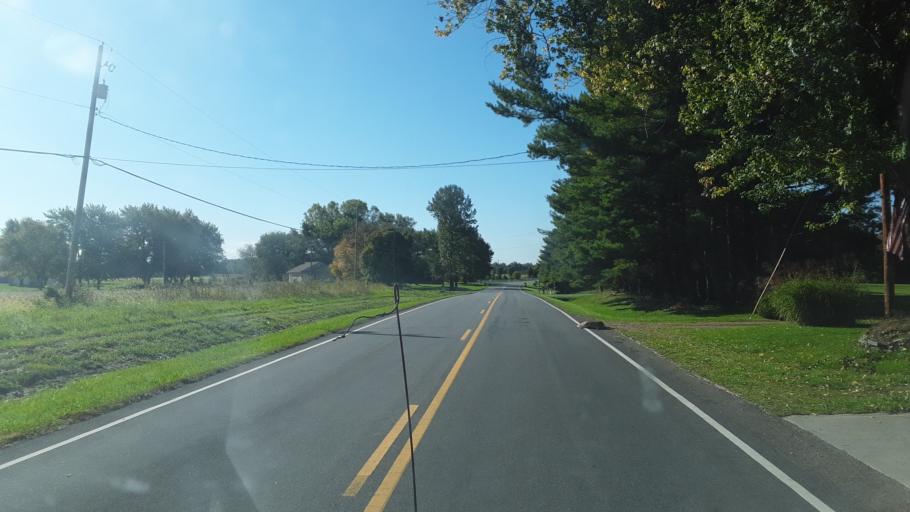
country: US
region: Ohio
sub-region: Delaware County
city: Sunbury
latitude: 40.2338
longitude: -82.7898
